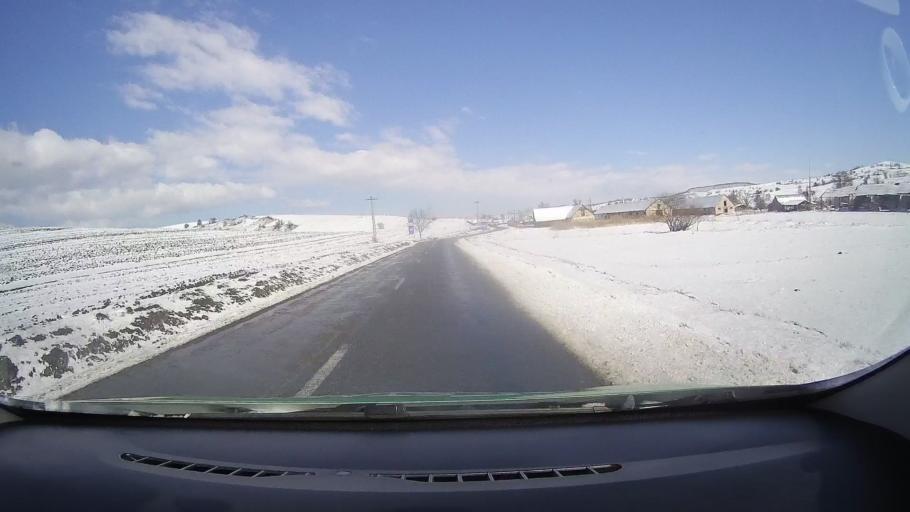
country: RO
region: Sibiu
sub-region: Comuna Vurpar
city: Vurpar
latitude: 45.8837
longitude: 24.3283
